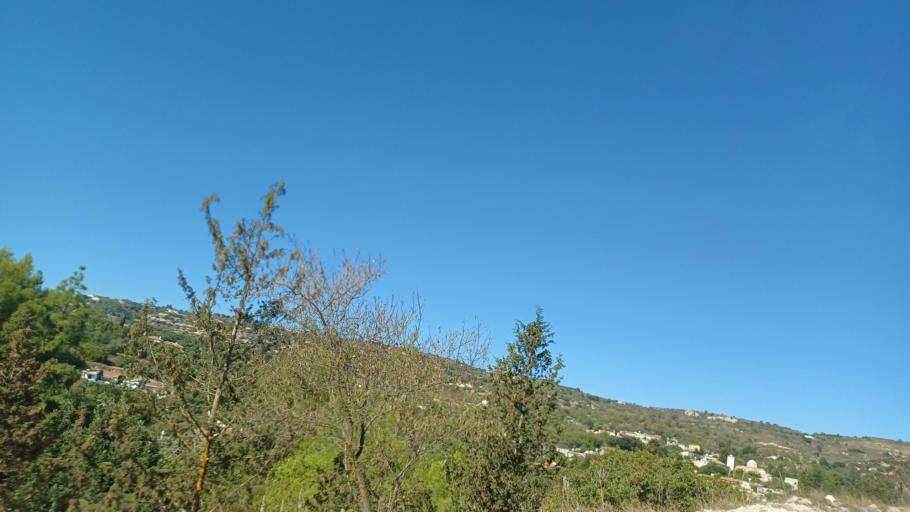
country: CY
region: Pafos
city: Mesogi
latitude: 34.8561
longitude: 32.5175
